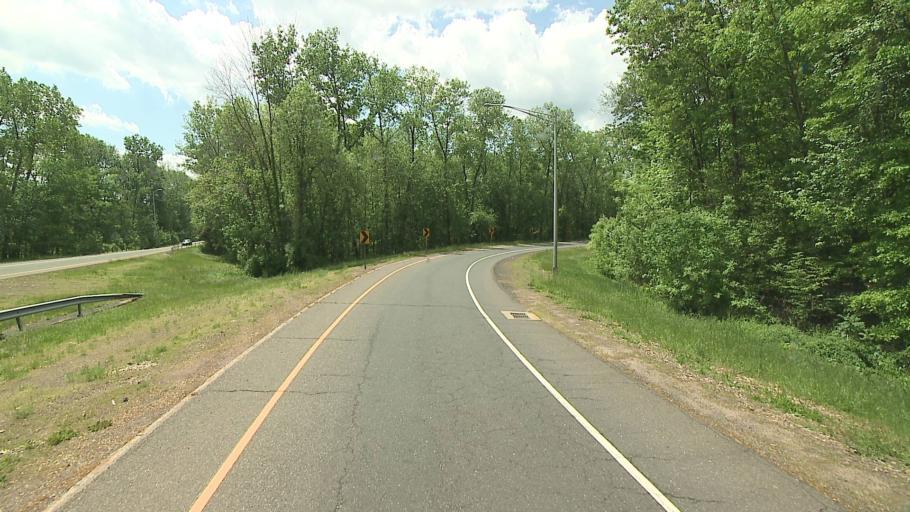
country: US
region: Connecticut
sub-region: Hartford County
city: Farmington
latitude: 41.7045
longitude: -72.8015
